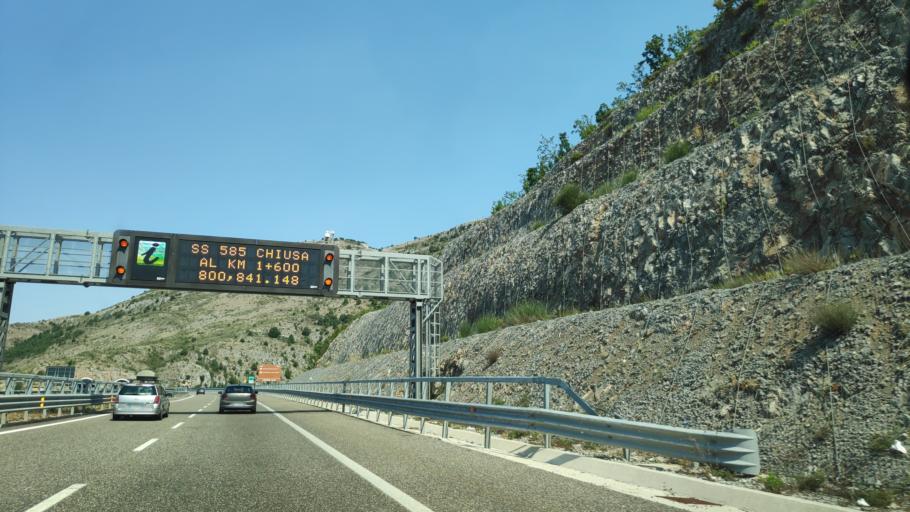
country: IT
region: Basilicate
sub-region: Provincia di Potenza
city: Lauria
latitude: 40.0326
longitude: 15.8746
